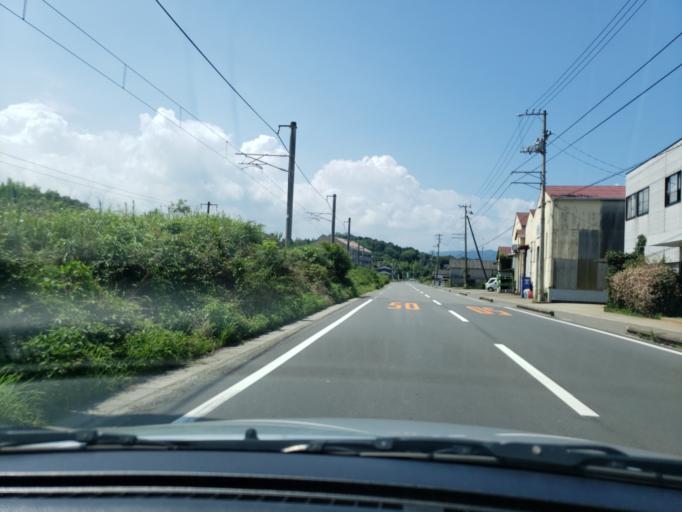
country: JP
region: Ehime
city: Hojo
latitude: 34.0913
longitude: 132.9326
